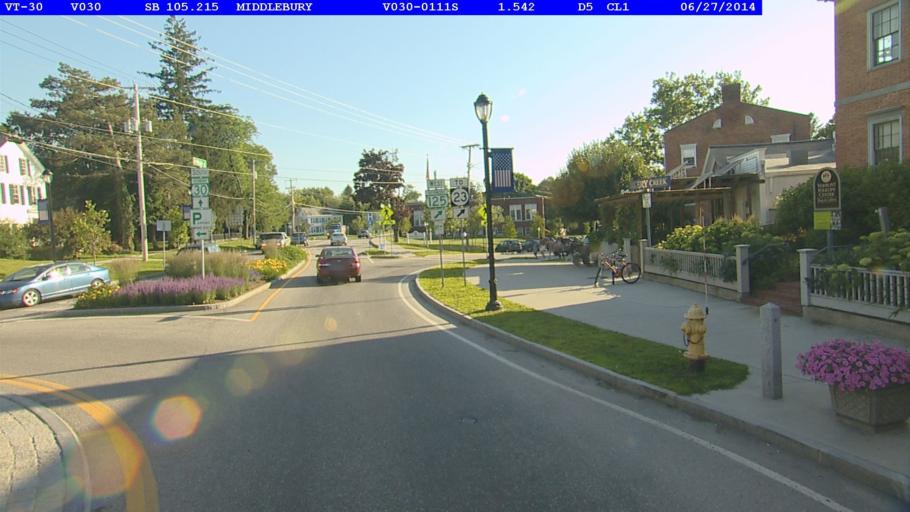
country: US
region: Vermont
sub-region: Addison County
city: Middlebury (village)
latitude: 44.0121
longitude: -73.1697
